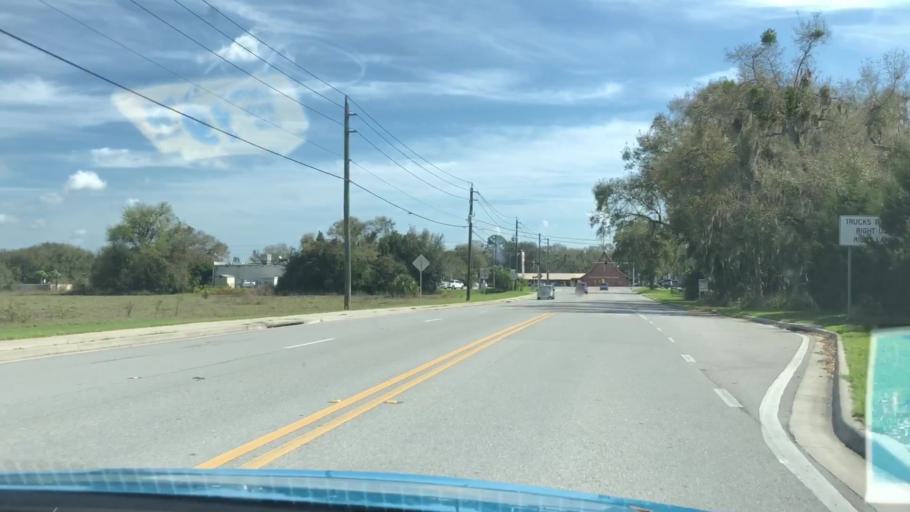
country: US
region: Florida
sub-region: Seminole County
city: Midway
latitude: 28.8502
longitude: -81.1644
